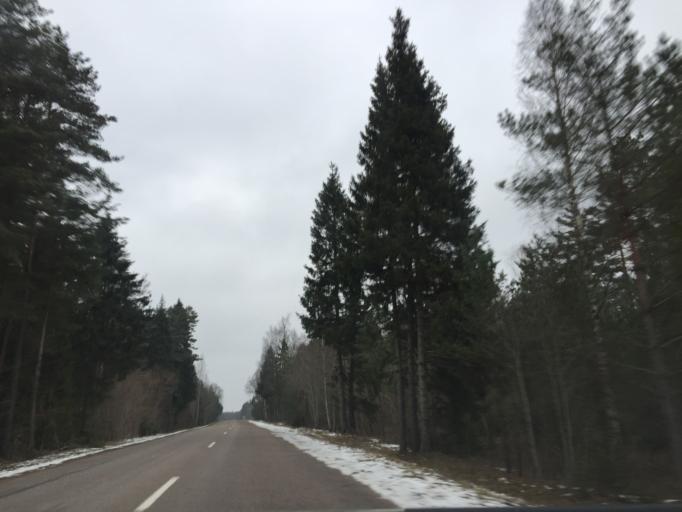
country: EE
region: Saare
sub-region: Kuressaare linn
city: Kuressaare
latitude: 58.3746
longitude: 22.2340
